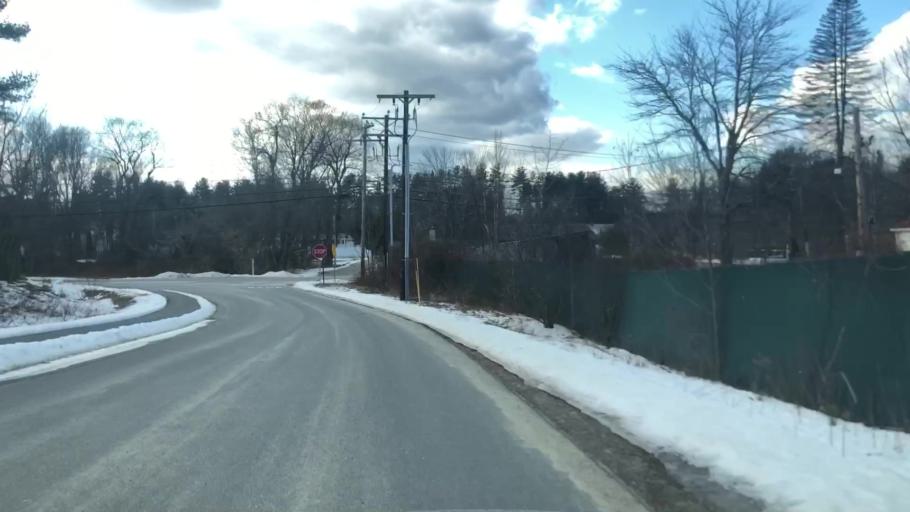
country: US
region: New Hampshire
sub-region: Hillsborough County
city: Milford
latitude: 42.8461
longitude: -71.6597
